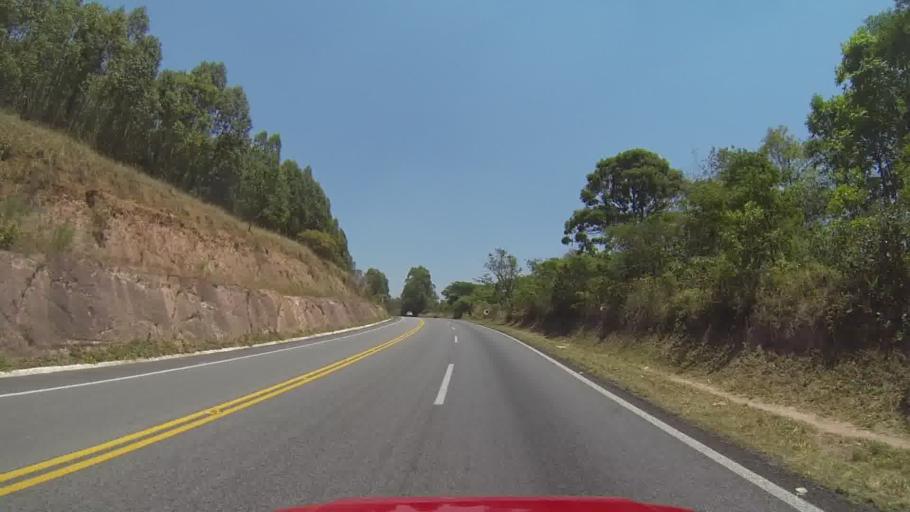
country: BR
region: Minas Gerais
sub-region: Itapecerica
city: Itapecerica
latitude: -20.2591
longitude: -45.1024
